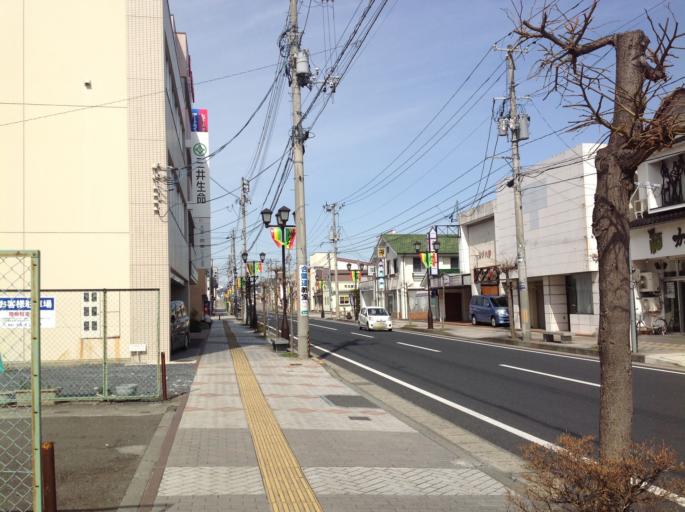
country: JP
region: Iwate
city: Ichinoseki
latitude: 38.9317
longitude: 141.1359
